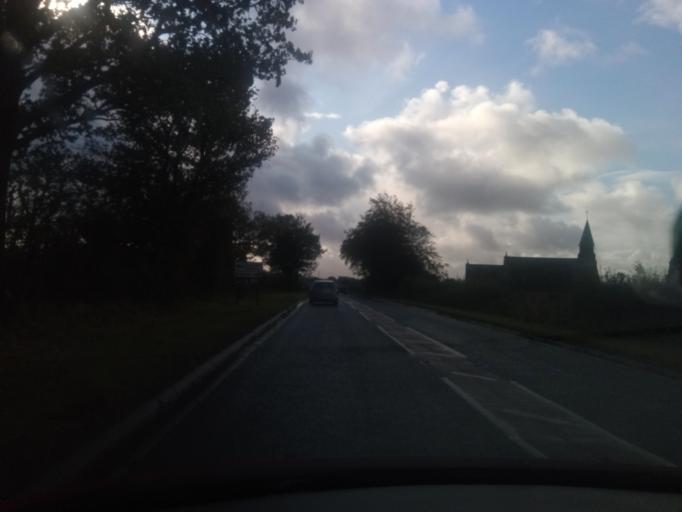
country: GB
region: England
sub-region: Cumbria
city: Carlisle
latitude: 54.9542
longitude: -2.9438
